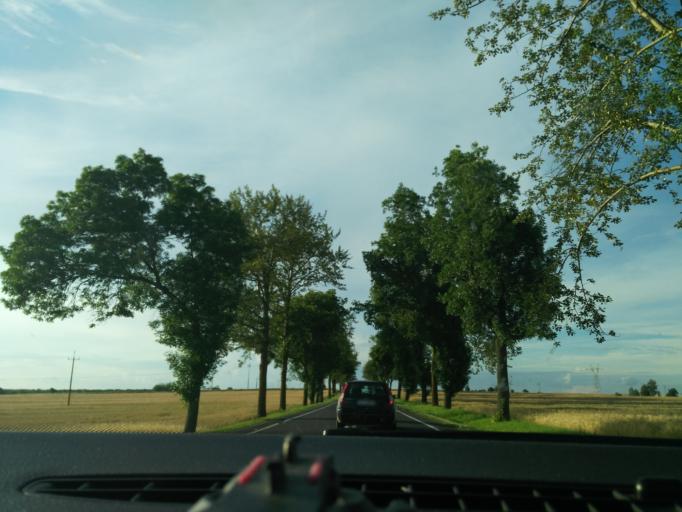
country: PL
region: Lublin Voivodeship
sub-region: Powiat krasnicki
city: Szastarka
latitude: 50.8100
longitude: 22.3196
